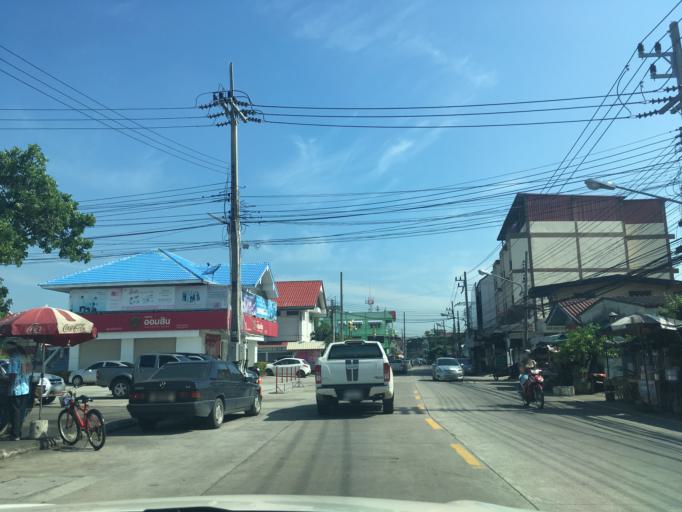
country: TH
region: Chon Buri
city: Chon Buri
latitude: 13.3850
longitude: 100.9872
